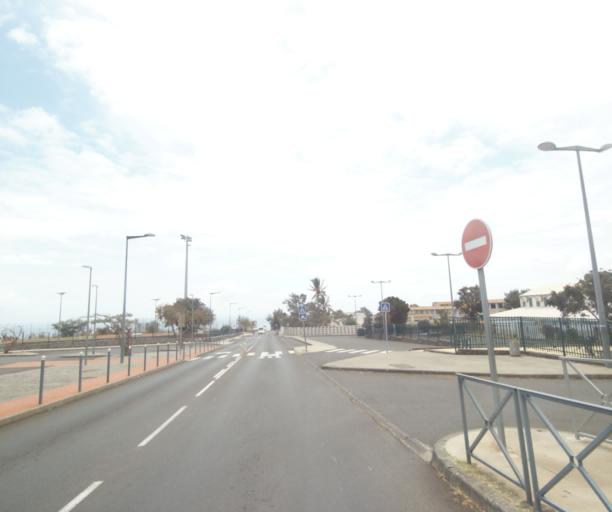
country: RE
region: Reunion
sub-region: Reunion
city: Saint-Paul
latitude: -21.0286
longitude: 55.2696
